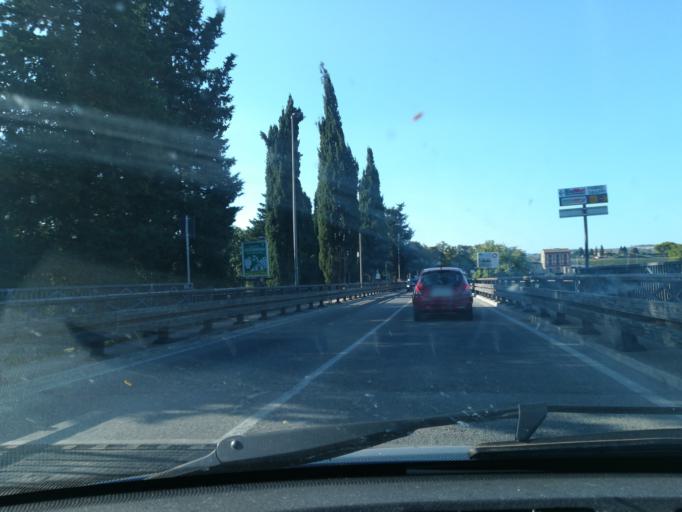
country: IT
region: The Marches
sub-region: Provincia di Macerata
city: Villa Potenza
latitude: 43.3274
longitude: 13.4259
